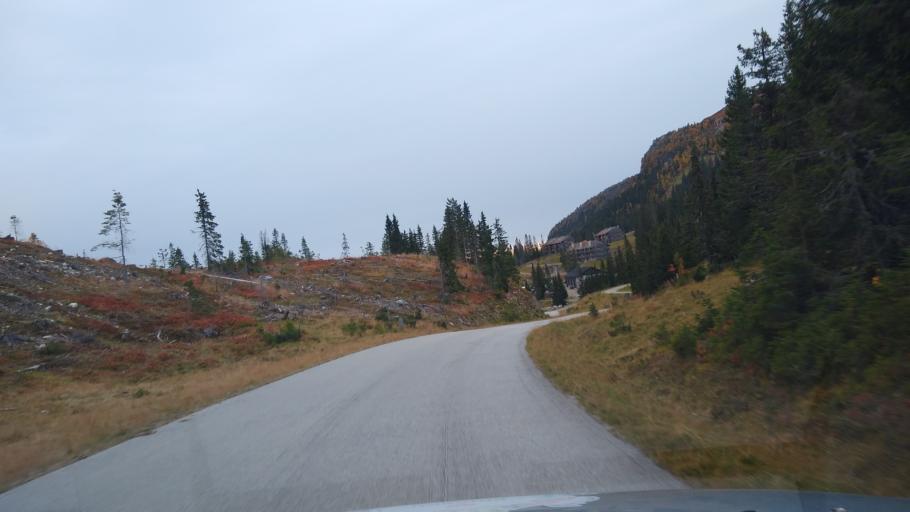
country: NO
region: Oppland
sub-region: Ringebu
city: Ringebu
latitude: 61.4761
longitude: 10.1280
